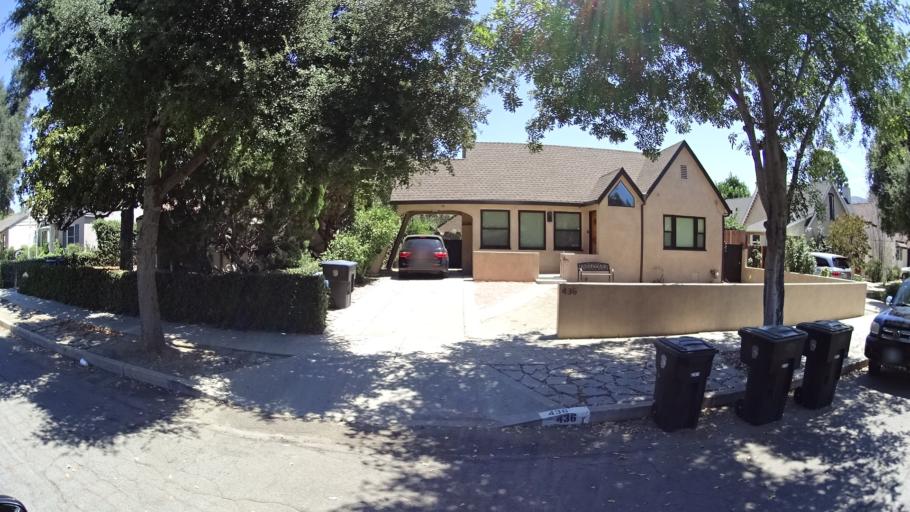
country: US
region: California
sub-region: Los Angeles County
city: Universal City
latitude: 34.1503
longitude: -118.3324
